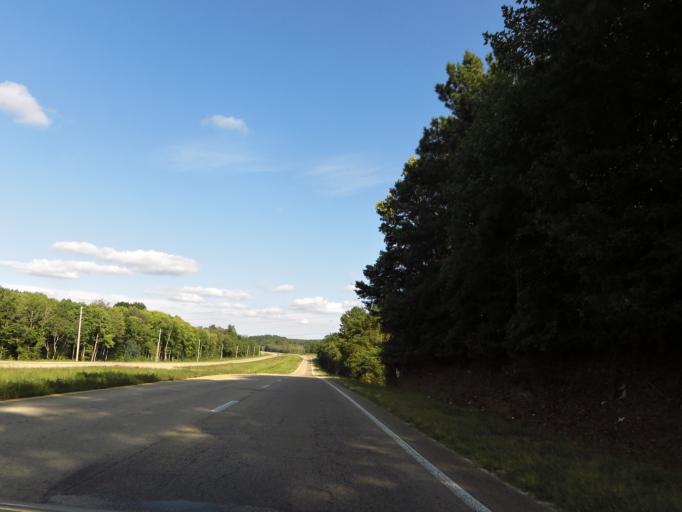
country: US
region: Mississippi
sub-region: Alcorn County
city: Farmington
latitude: 34.8585
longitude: -88.3962
